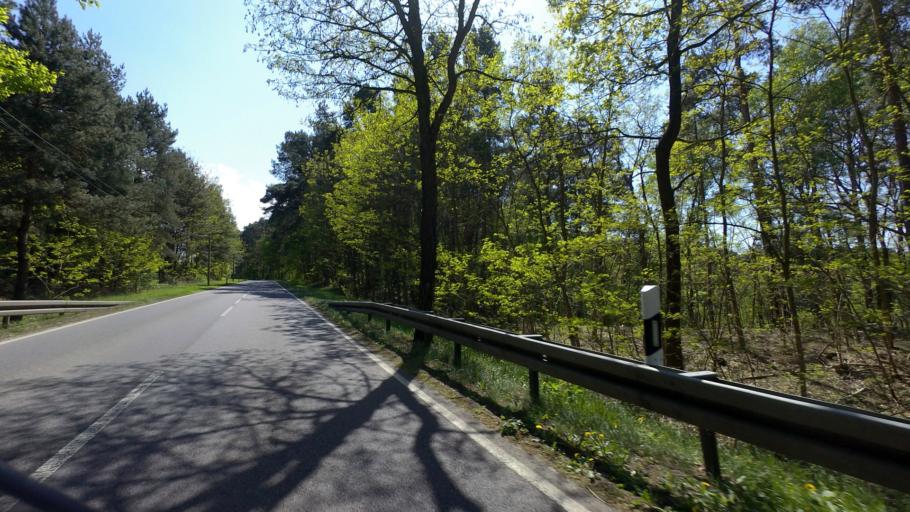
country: DE
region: Brandenburg
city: Lieberose
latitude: 51.9952
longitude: 14.2039
